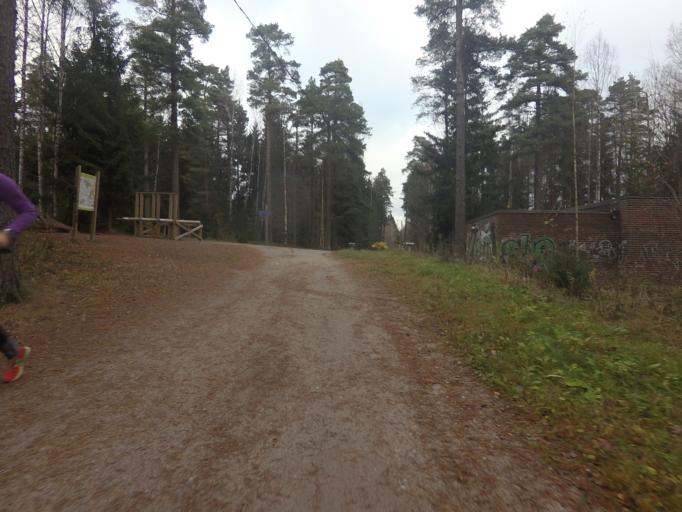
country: FI
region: Uusimaa
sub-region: Helsinki
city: Kauniainen
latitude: 60.1875
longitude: 24.6938
